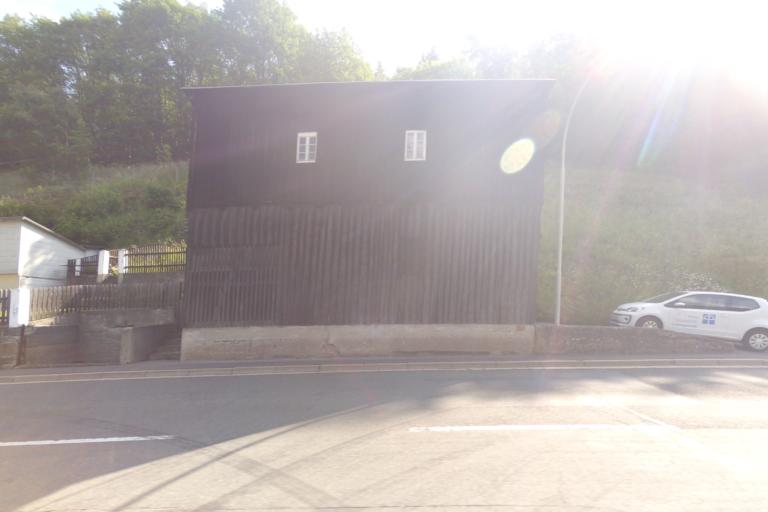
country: DE
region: Bavaria
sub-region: Upper Franconia
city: Ludwigsstadt
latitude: 50.4951
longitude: 11.3775
